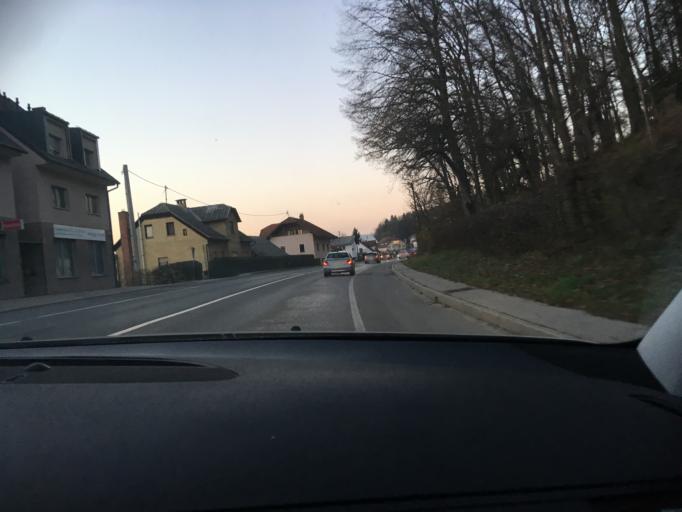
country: SI
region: Skofljica
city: Skofljica
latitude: 45.9880
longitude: 14.5677
